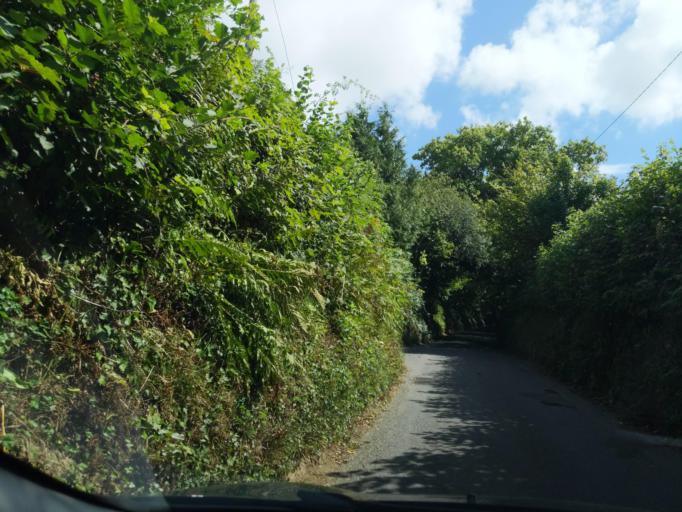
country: GB
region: England
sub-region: Devon
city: Modbury
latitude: 50.3639
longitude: -3.9002
